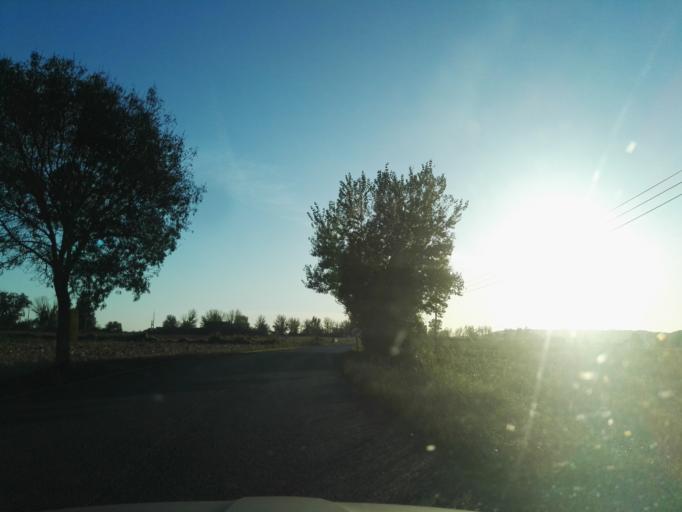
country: PT
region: Santarem
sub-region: Alpiarca
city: Alpiarca
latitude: 39.3417
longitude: -8.5597
